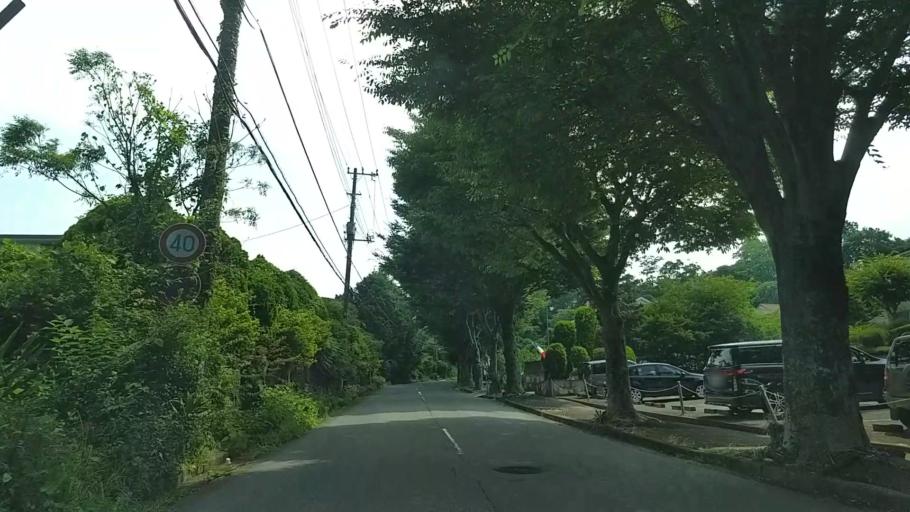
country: JP
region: Shizuoka
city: Ito
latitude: 34.9209
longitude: 139.1057
